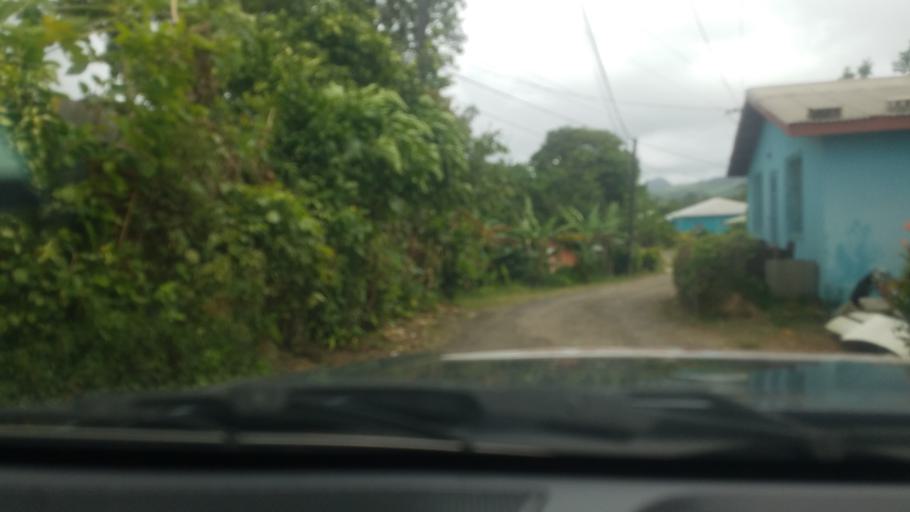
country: LC
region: Micoud Quarter
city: Micoud
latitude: 13.8049
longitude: -60.9438
